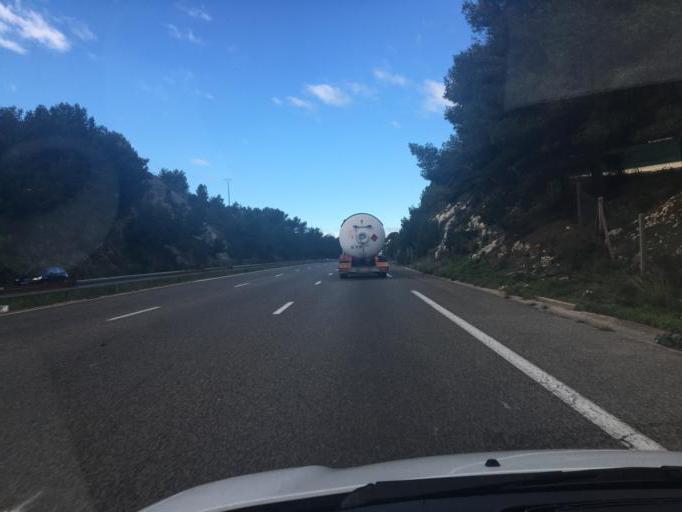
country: FR
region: Provence-Alpes-Cote d'Azur
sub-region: Departement des Bouches-du-Rhone
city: Martigues
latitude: 43.3956
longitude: 5.0680
